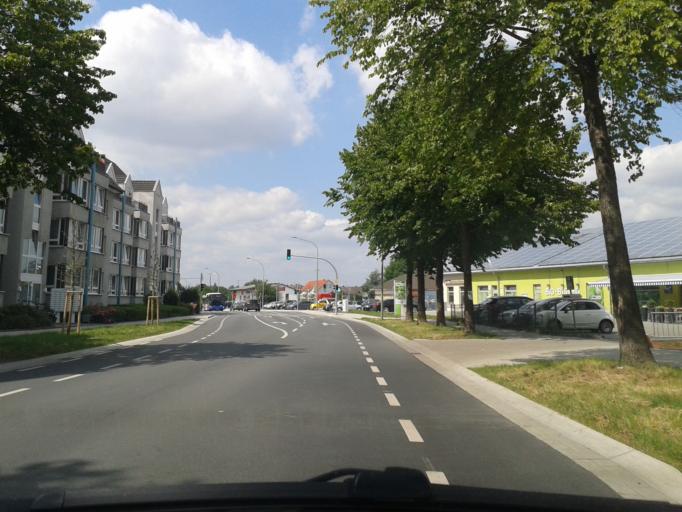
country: DE
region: North Rhine-Westphalia
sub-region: Regierungsbezirk Detmold
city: Paderborn
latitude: 51.7268
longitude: 8.7591
